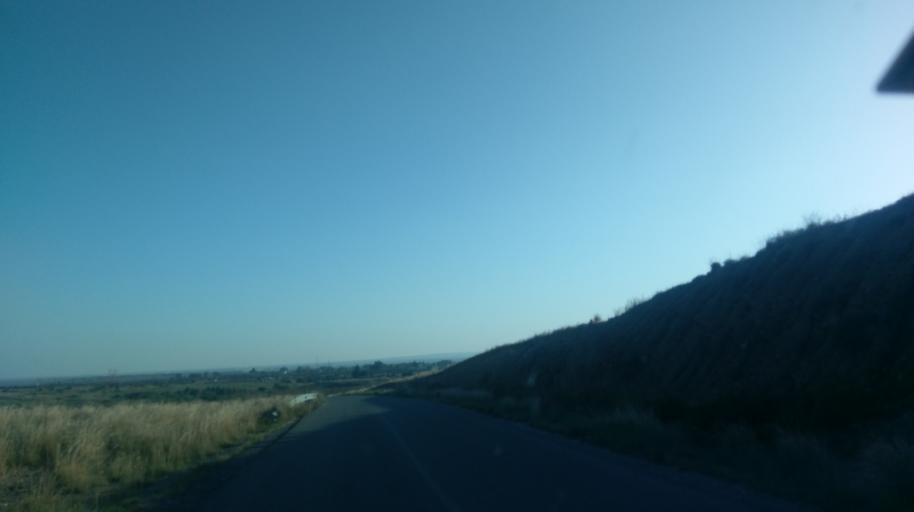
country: CY
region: Ammochostos
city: Lefkonoiko
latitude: 35.2814
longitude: 33.6580
